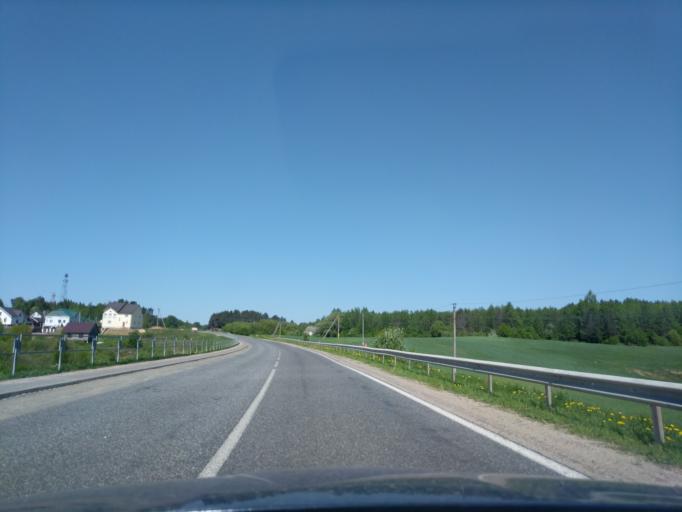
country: BY
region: Minsk
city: Myadzyel
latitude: 54.8918
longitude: 26.9120
